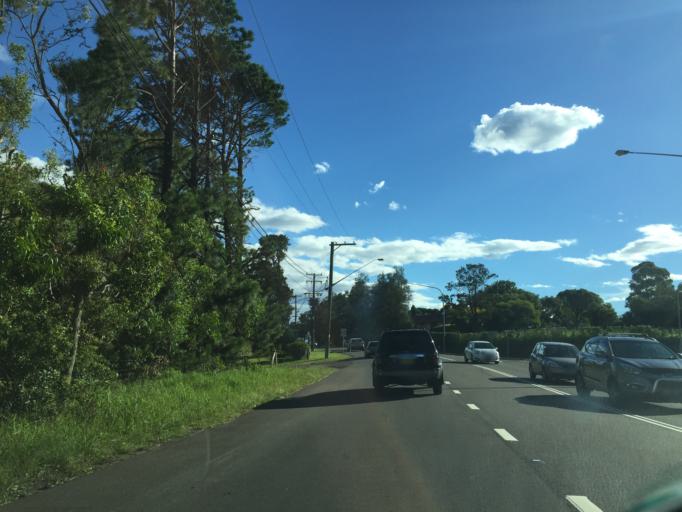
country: AU
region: New South Wales
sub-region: Hornsby Shire
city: Galston
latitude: -33.6789
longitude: 151.0300
